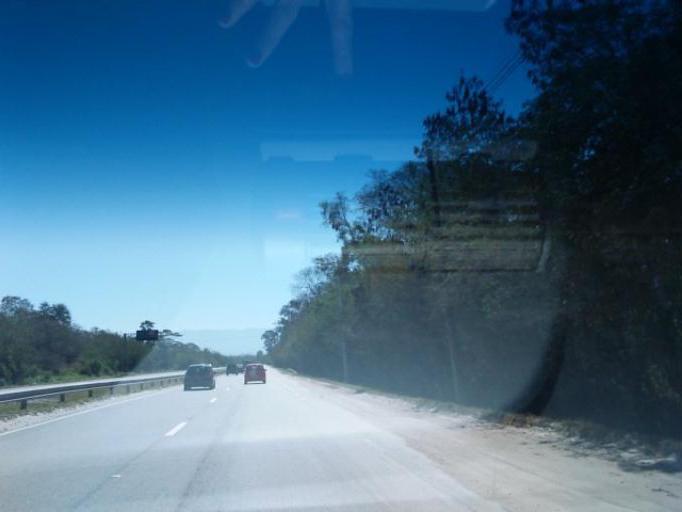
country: BR
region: Sao Paulo
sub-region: Taubate
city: Taubate
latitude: -23.0109
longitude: -45.6409
